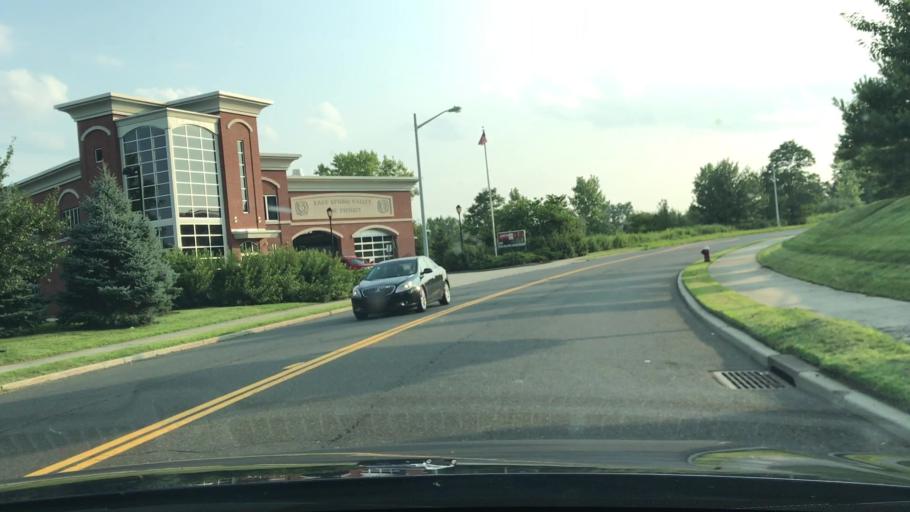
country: US
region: New York
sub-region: Rockland County
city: Spring Valley
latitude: 41.1092
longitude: -74.0219
